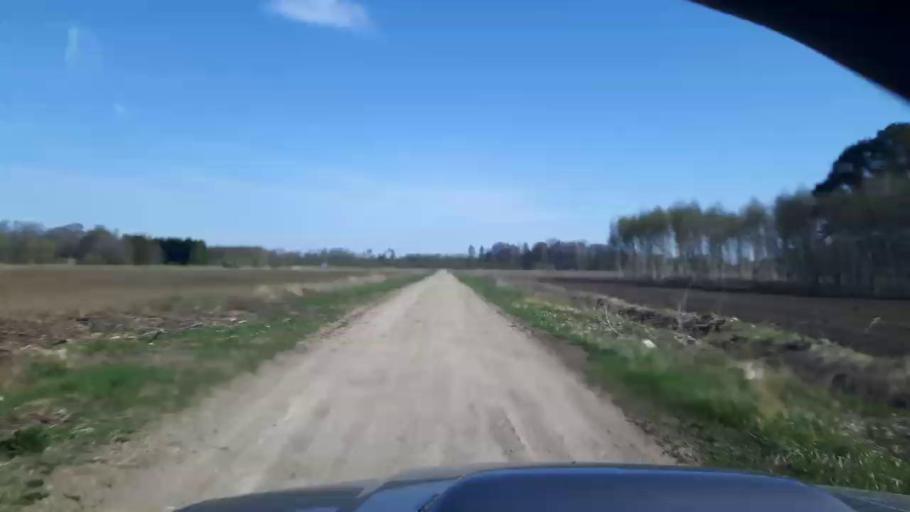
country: EE
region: Paernumaa
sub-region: Tootsi vald
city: Tootsi
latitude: 58.5225
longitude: 24.9295
